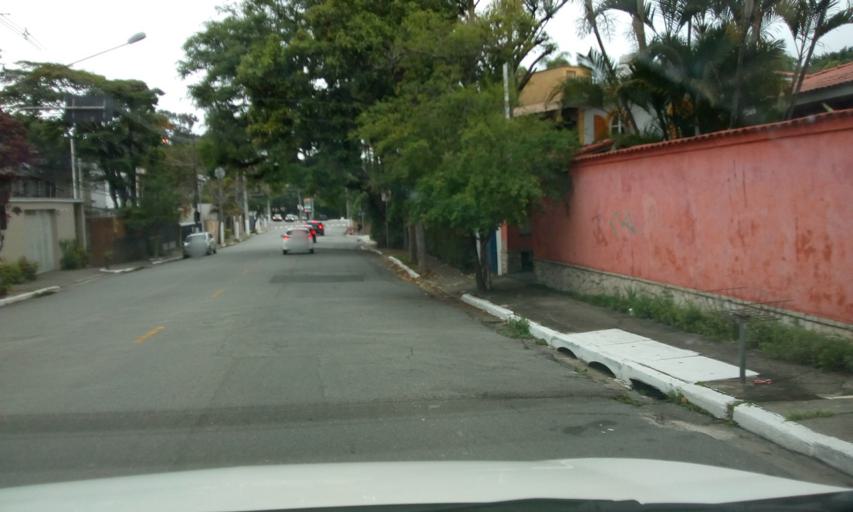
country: BR
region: Sao Paulo
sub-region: Sao Paulo
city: Sao Paulo
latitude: -23.5490
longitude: -46.6862
